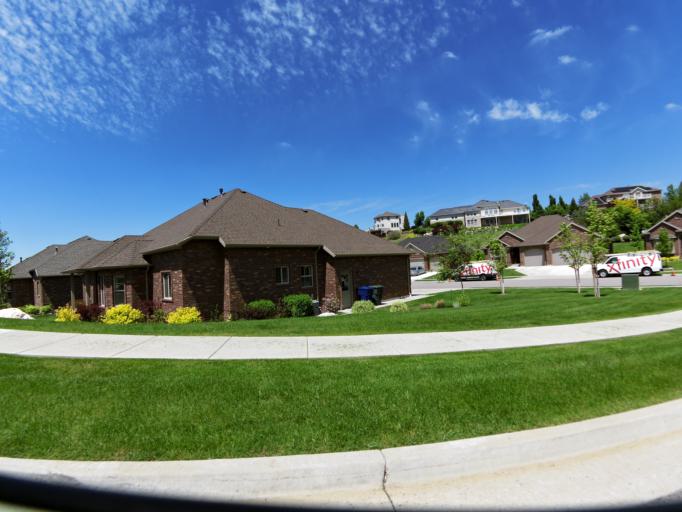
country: US
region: Utah
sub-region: Weber County
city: Uintah
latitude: 41.1625
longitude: -111.9282
